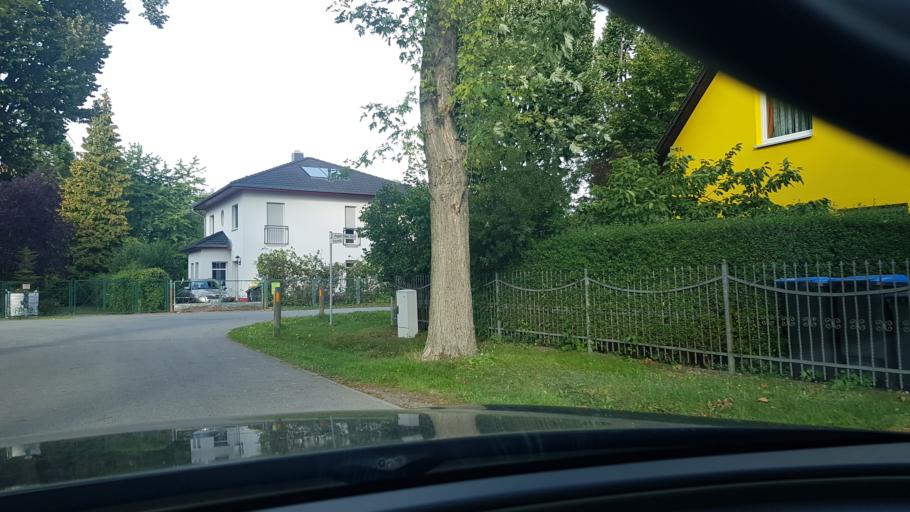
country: DE
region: Brandenburg
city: Brieselang
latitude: 52.5803
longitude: 13.0060
